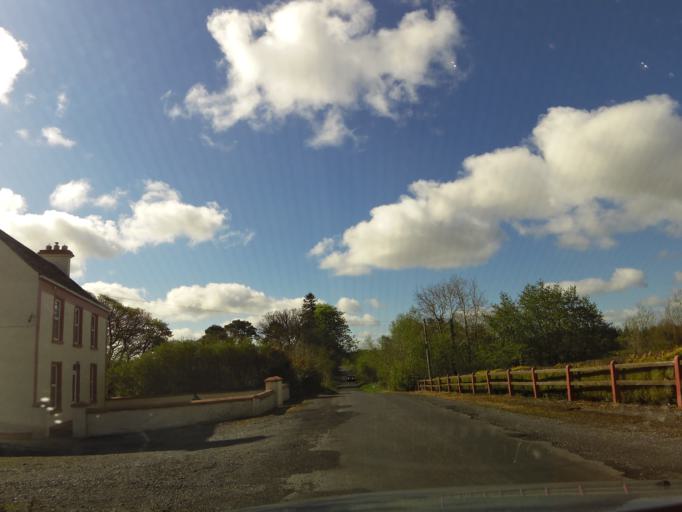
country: IE
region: Connaught
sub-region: Maigh Eo
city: Claremorris
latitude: 53.7814
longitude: -8.9607
